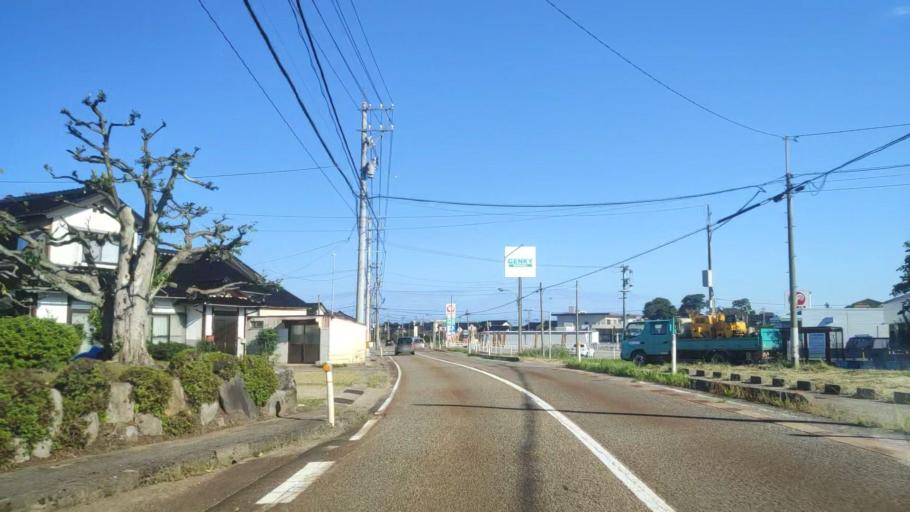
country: JP
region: Ishikawa
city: Hakui
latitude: 36.8192
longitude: 136.7579
